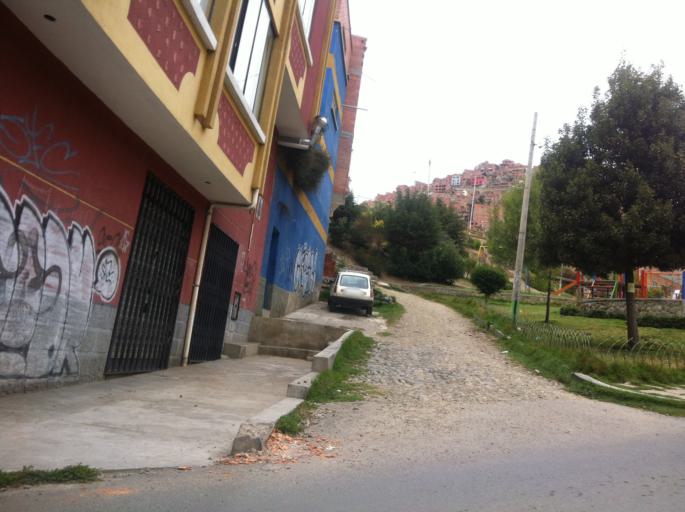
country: BO
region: La Paz
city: La Paz
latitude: -16.4780
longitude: -68.1229
